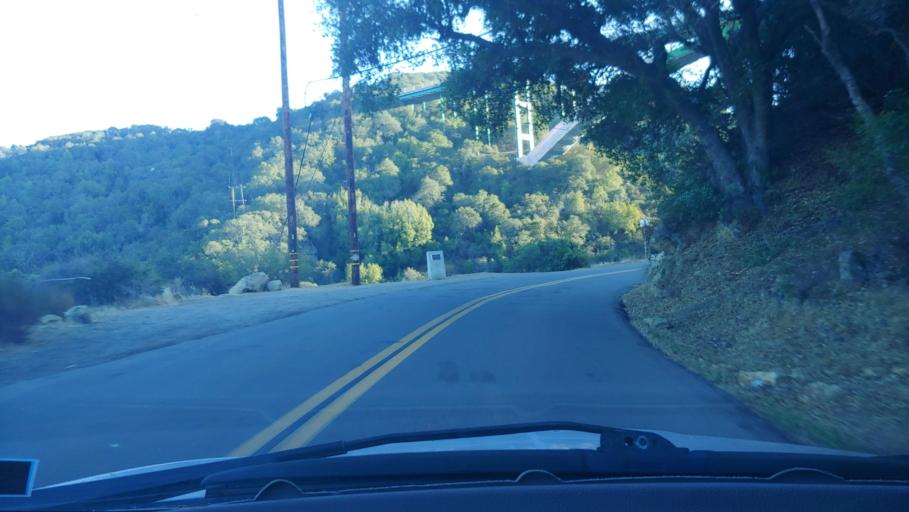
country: US
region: California
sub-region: Santa Barbara County
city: Goleta
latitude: 34.5282
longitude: -119.8332
